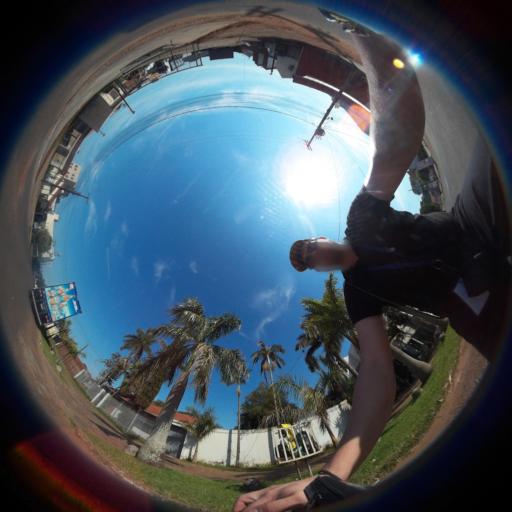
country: BR
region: Mato Grosso do Sul
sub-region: Ponta Pora
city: Ponta Pora
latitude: -22.5437
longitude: -55.7247
